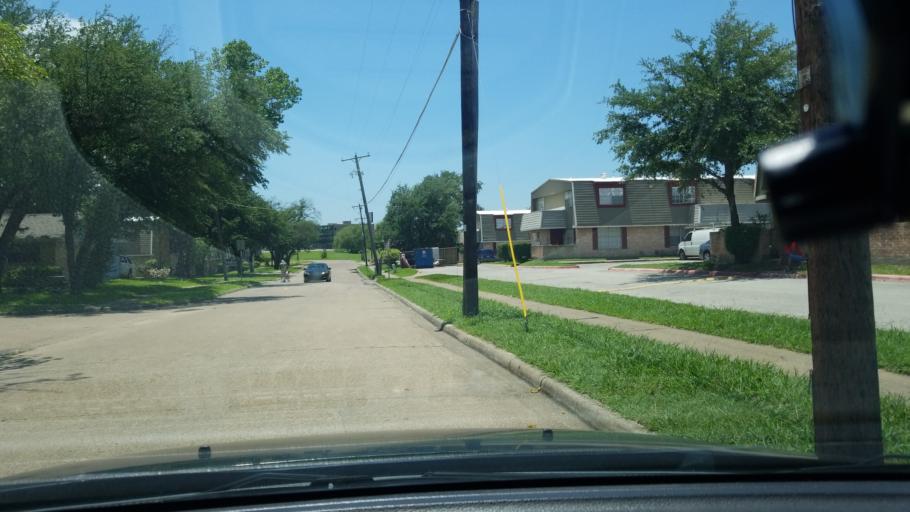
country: US
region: Texas
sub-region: Dallas County
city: Mesquite
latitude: 32.7961
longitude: -96.6507
